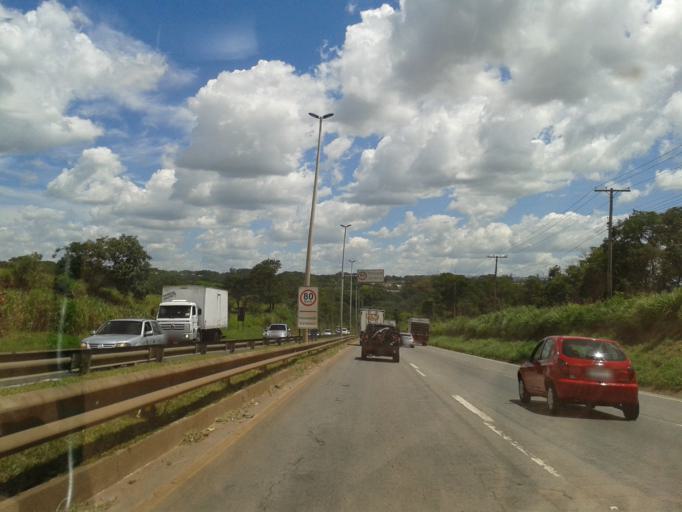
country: BR
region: Goias
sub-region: Aparecida De Goiania
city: Aparecida de Goiania
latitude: -16.7724
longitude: -49.2383
